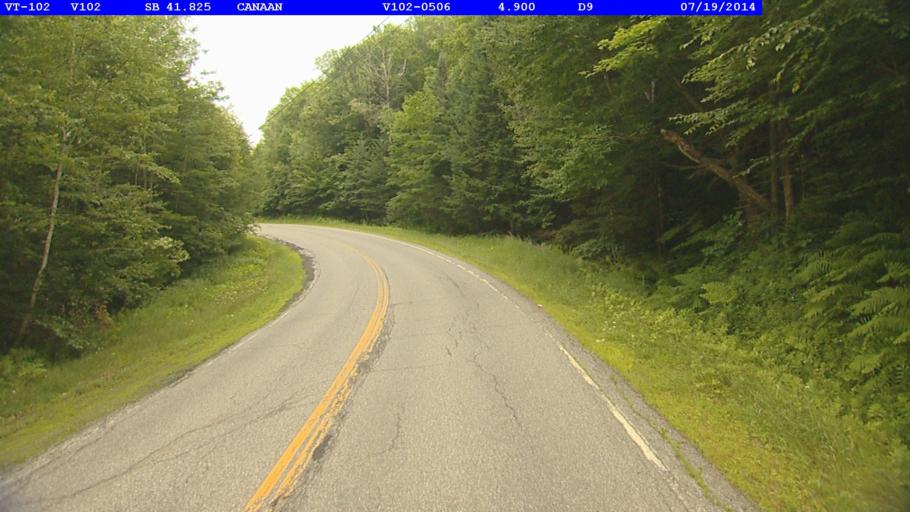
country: US
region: New Hampshire
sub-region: Coos County
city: Colebrook
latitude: 44.9724
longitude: -71.5325
